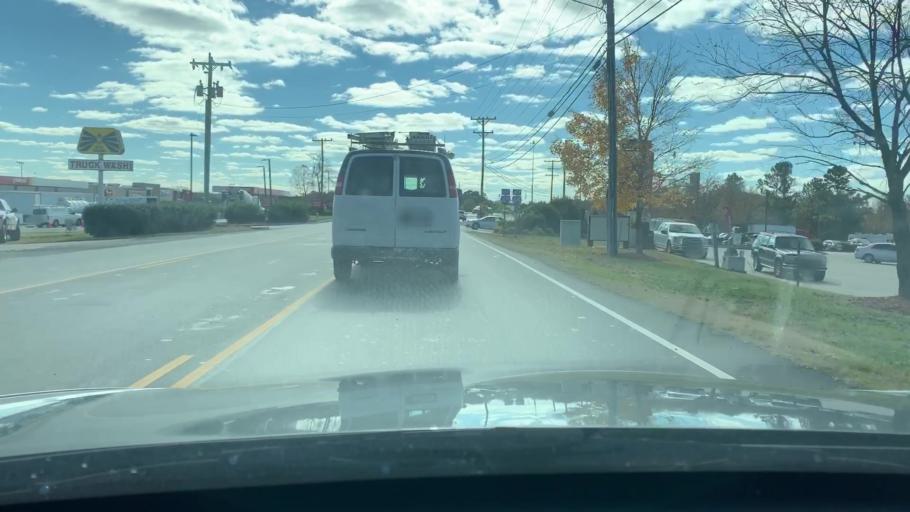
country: US
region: North Carolina
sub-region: Alamance County
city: Haw River
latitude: 36.0720
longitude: -79.3519
